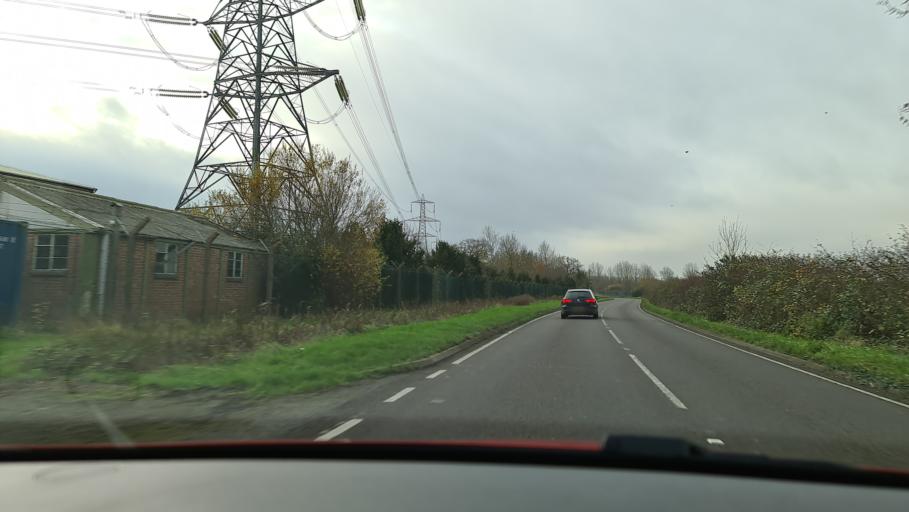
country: GB
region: England
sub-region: Oxfordshire
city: Bicester
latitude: 51.8574
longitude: -1.0893
